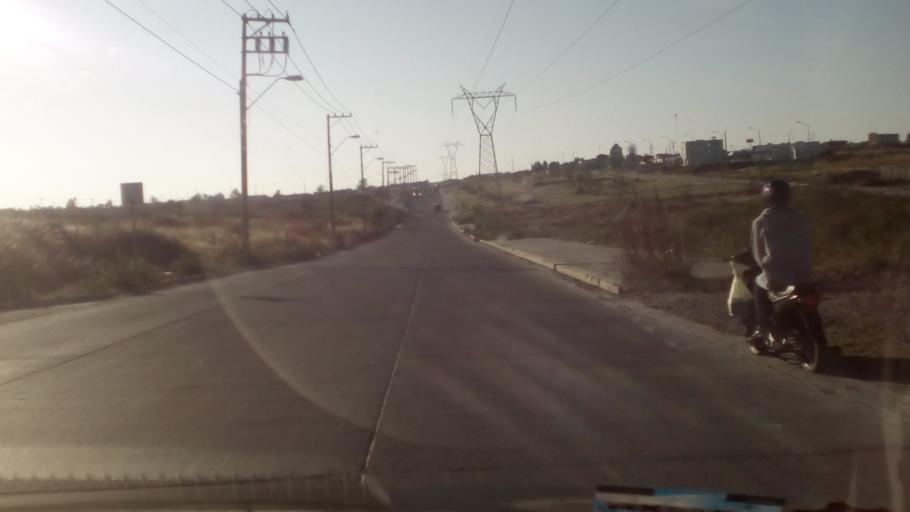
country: MX
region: Guanajuato
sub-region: Leon
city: Fraccionamiento Paseo de las Torres
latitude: 21.1743
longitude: -101.7643
